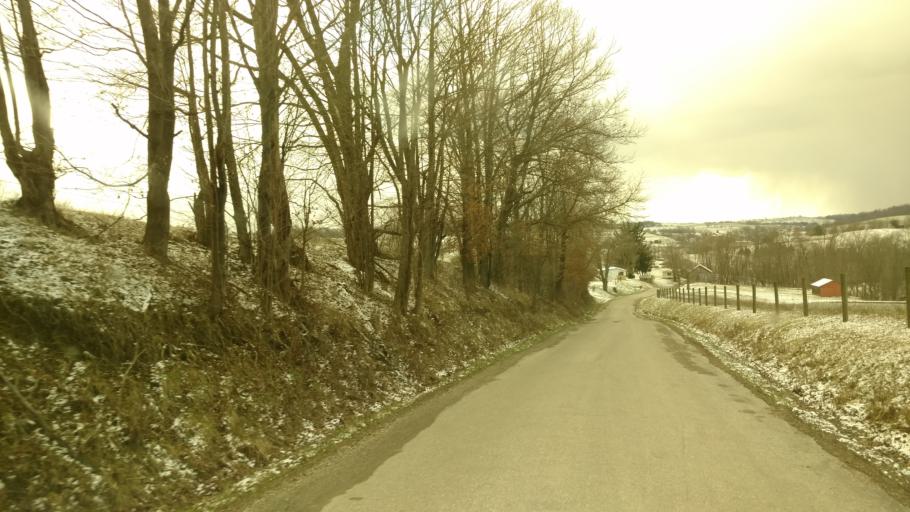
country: US
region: Ohio
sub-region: Holmes County
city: Millersburg
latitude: 40.5186
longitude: -81.8107
